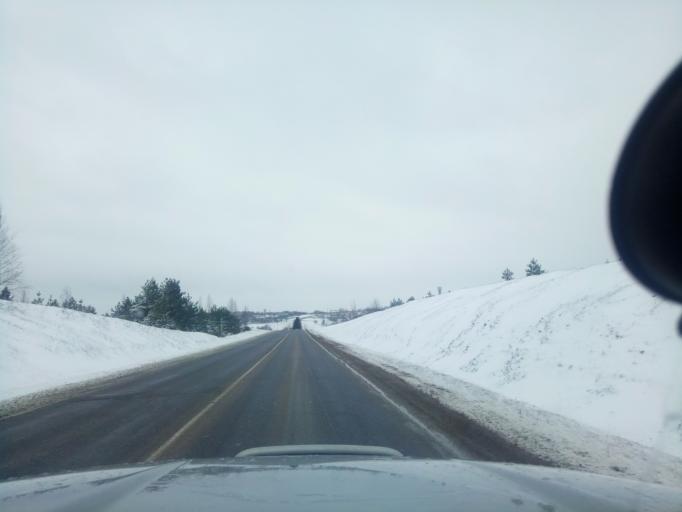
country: BY
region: Minsk
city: Kapyl'
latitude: 53.1407
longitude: 27.0839
